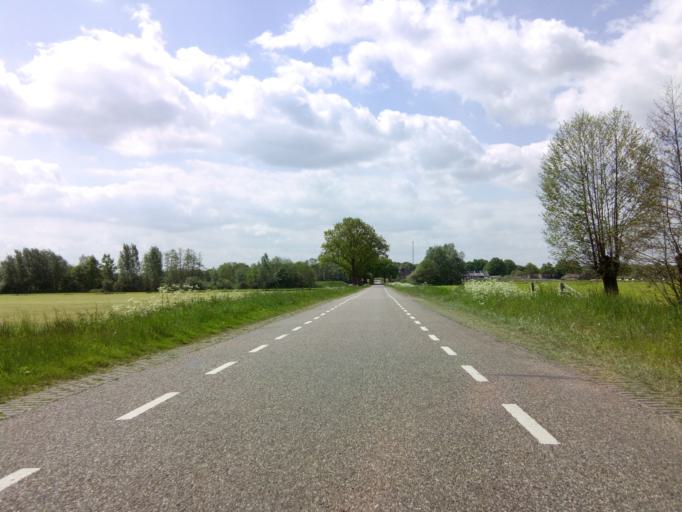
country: NL
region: Utrecht
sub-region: Gemeente Veenendaal
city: Veenendaal
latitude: 52.0559
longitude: 5.5353
